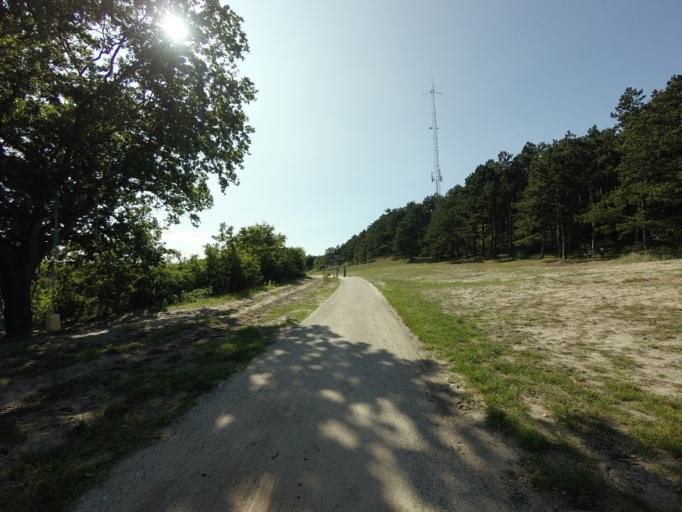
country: NL
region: Friesland
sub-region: Gemeente Terschelling
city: West-Terschelling
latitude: 53.4014
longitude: 5.3500
